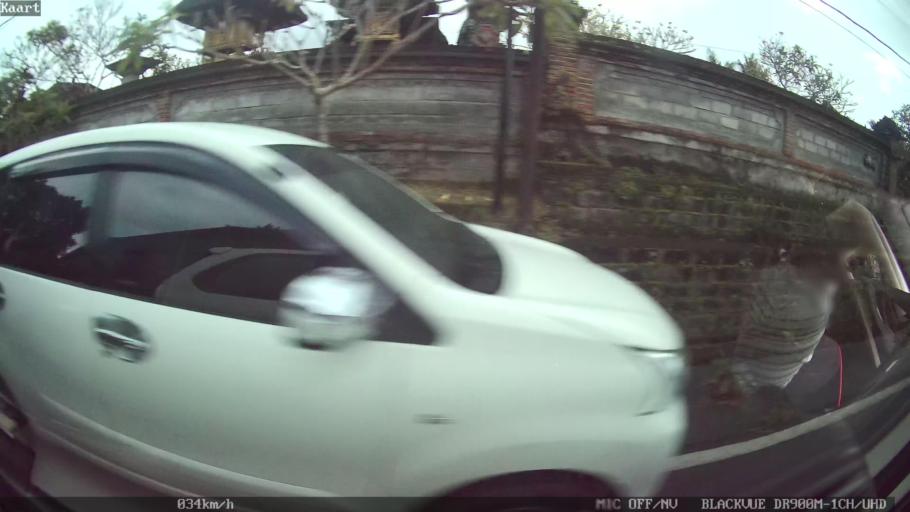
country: ID
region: Bali
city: Banjar Pande
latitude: -8.5218
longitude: 115.2282
